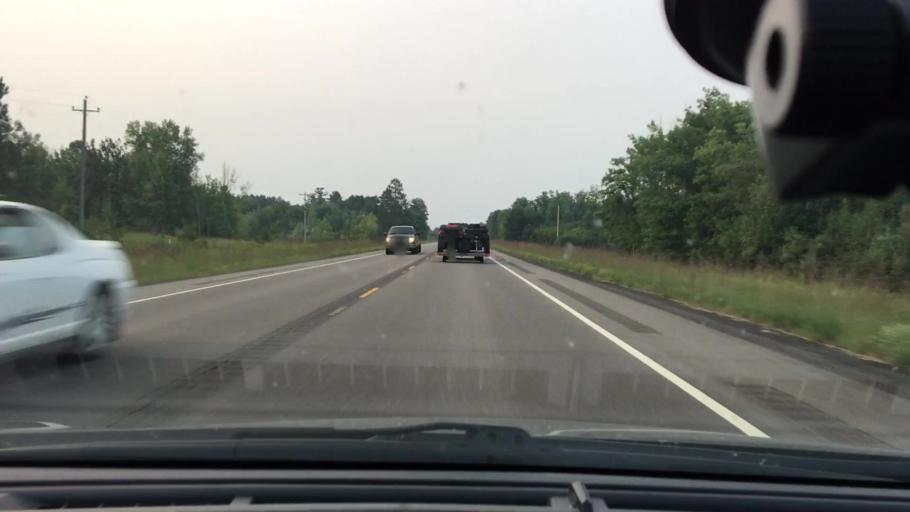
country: US
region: Minnesota
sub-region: Crow Wing County
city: Crosby
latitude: 46.5847
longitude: -93.9526
